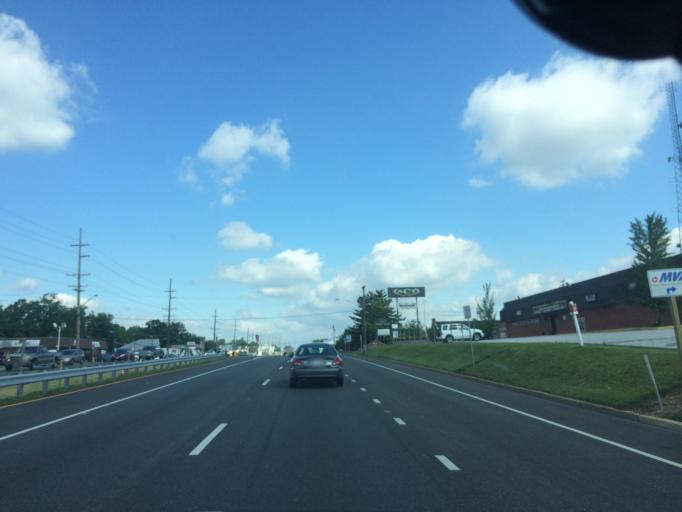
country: US
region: Maryland
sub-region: Carroll County
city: Westminster
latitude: 39.5536
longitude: -76.9560
